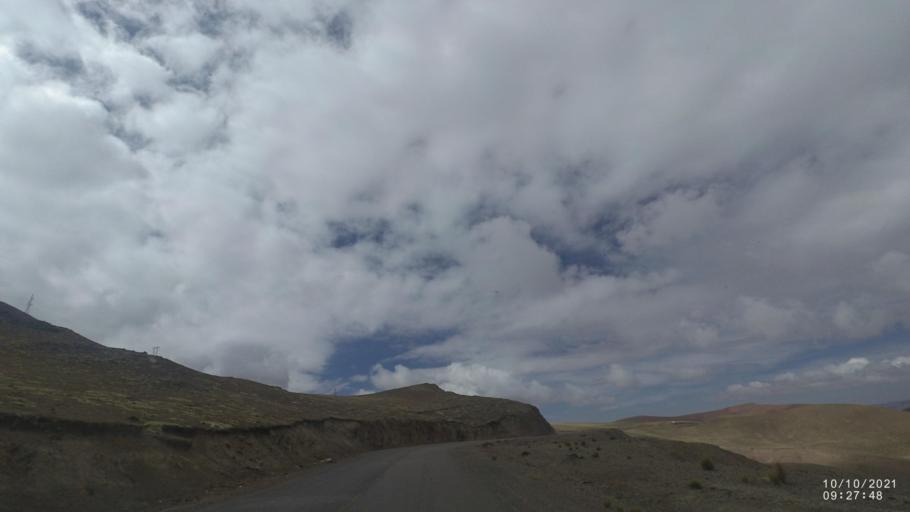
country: BO
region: La Paz
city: Quime
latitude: -17.1027
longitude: -67.3244
